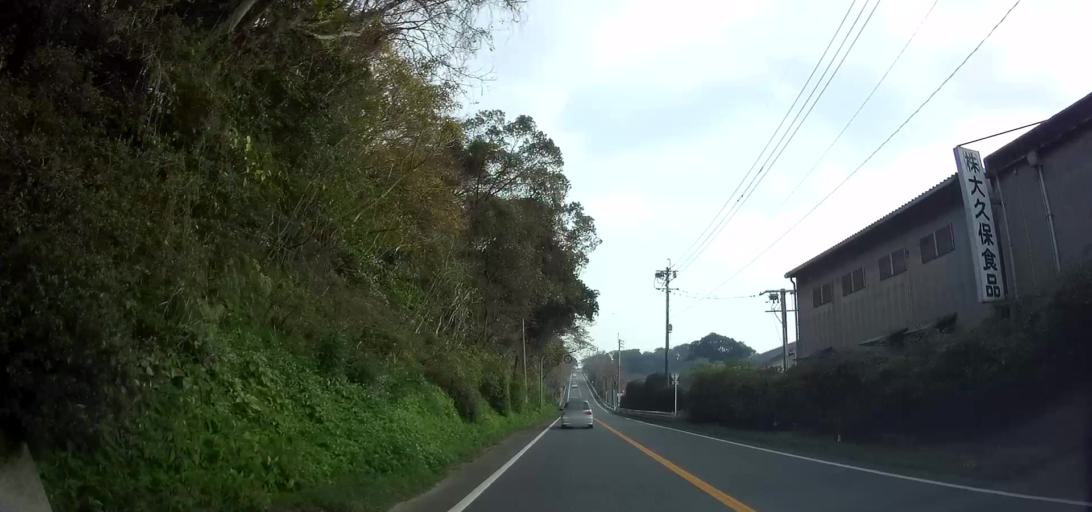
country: JP
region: Nagasaki
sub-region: Isahaya-shi
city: Isahaya
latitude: 32.7971
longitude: 130.1422
